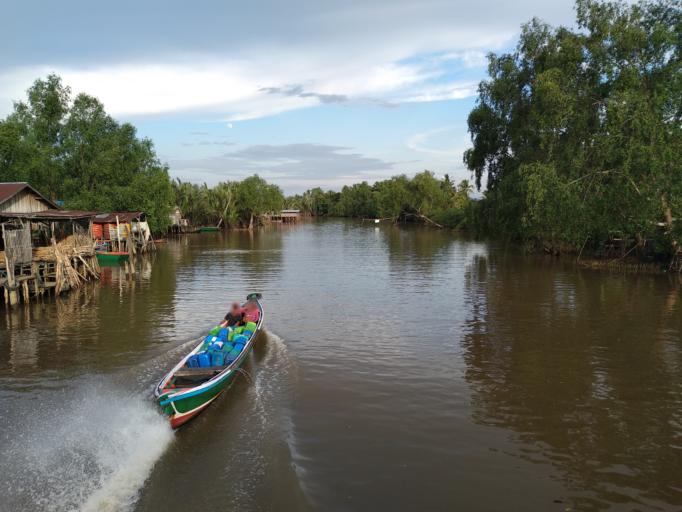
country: ID
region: South Kalimantan
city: Aluhaluh
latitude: -3.4699
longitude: 114.5313
